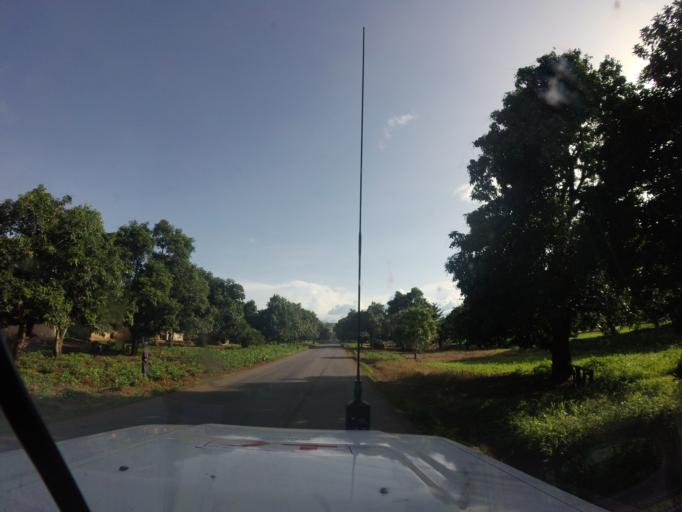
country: GN
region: Kindia
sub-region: Kindia
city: Kindia
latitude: 10.0100
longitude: -12.6919
